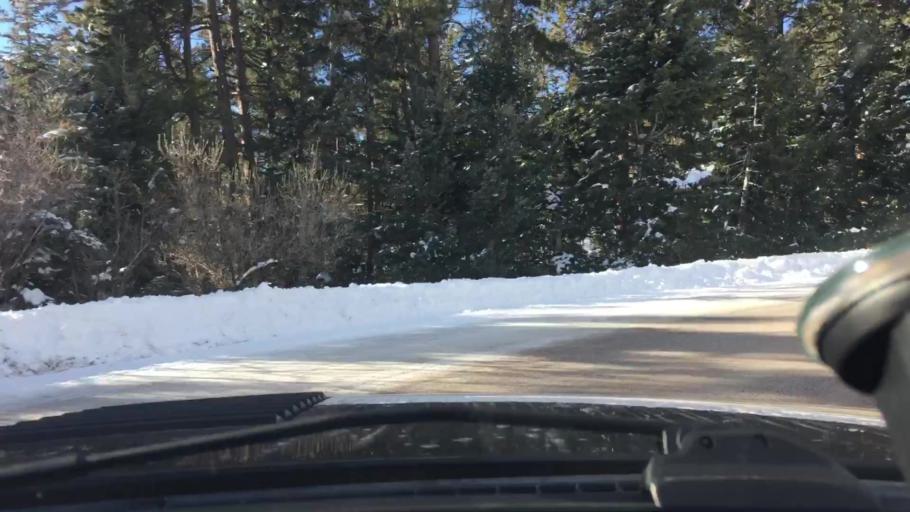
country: US
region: Colorado
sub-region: Jefferson County
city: Indian Hills
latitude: 39.5556
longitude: -105.2464
